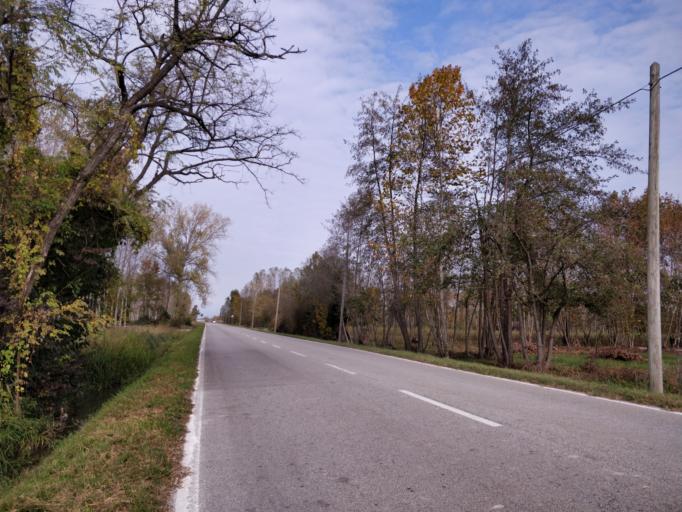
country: IT
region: Friuli Venezia Giulia
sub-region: Provincia di Udine
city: Bertiolo
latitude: 45.9212
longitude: 13.0481
